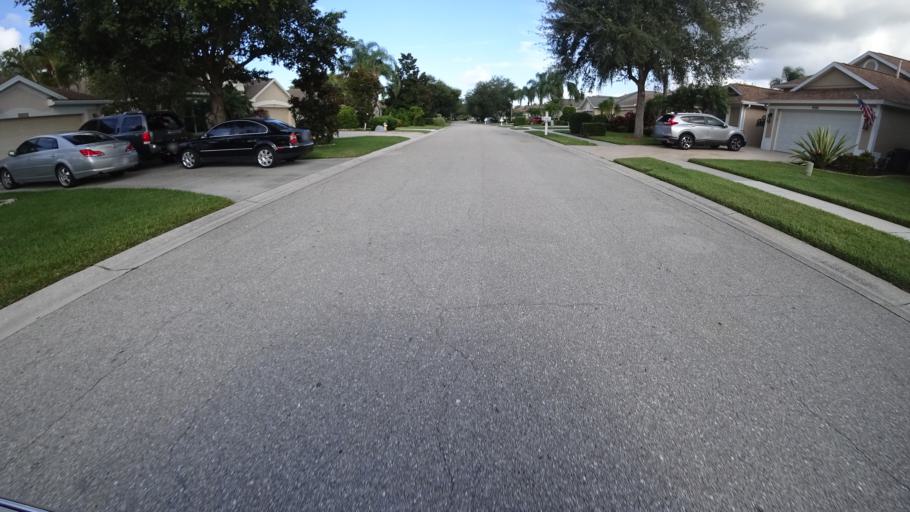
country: US
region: Florida
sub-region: Sarasota County
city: Desoto Lakes
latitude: 27.4221
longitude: -82.4913
